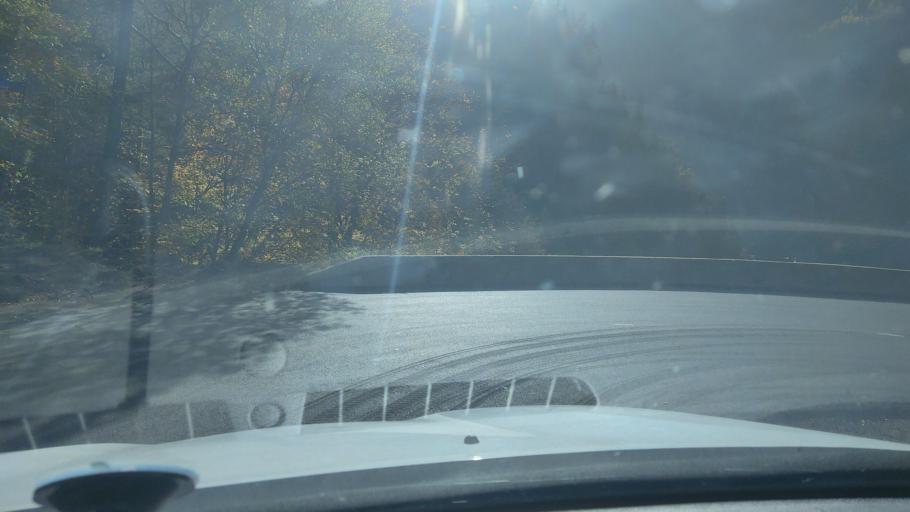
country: FR
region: Rhone-Alpes
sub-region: Departement de la Savoie
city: Saint-Jean-de-Maurienne
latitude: 45.2251
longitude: 6.3176
